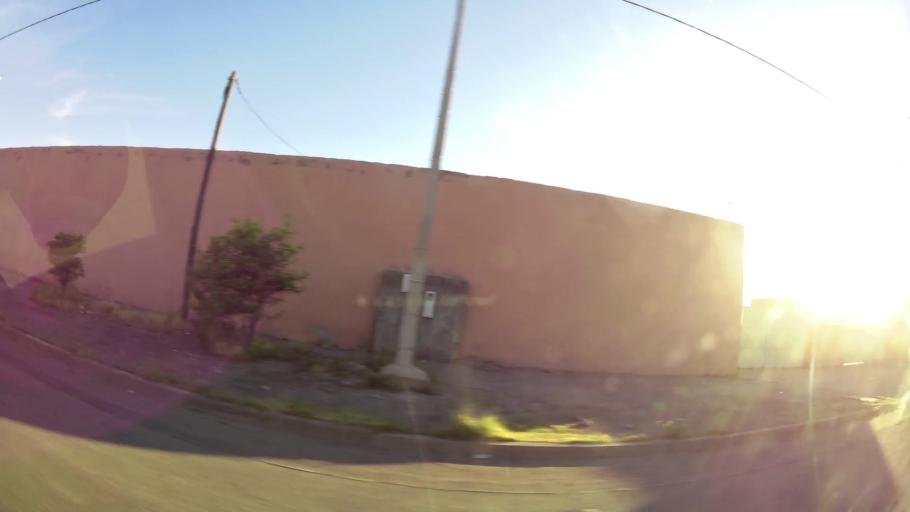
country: MA
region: Marrakech-Tensift-Al Haouz
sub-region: Marrakech
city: Marrakesh
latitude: 31.6672
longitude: -8.0372
